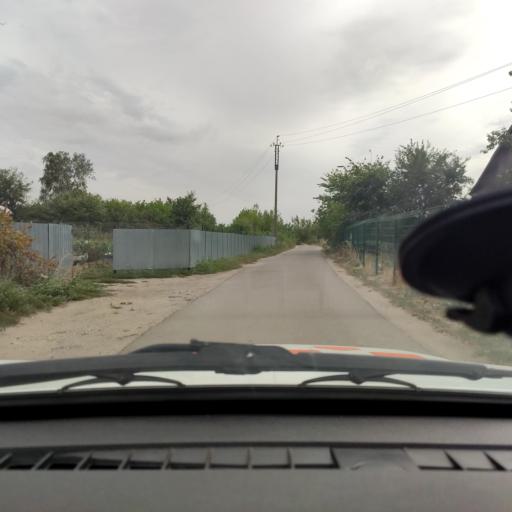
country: RU
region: Lipetsk
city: Khlevnoye
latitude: 52.0061
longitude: 39.1122
